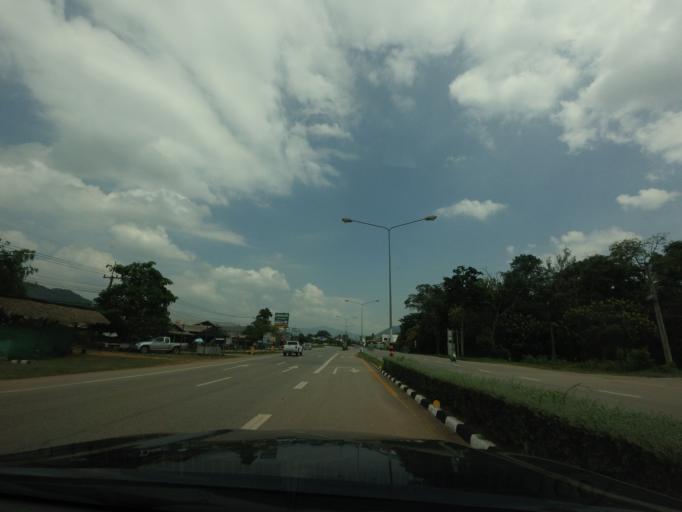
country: TH
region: Loei
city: Phu Ruea
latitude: 17.4493
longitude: 101.3558
